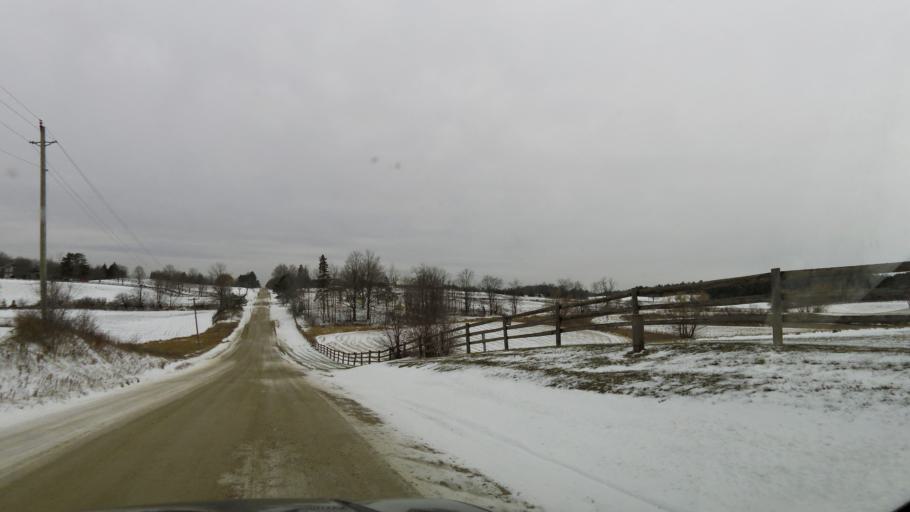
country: CA
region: Ontario
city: Vaughan
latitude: 43.9472
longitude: -79.6222
